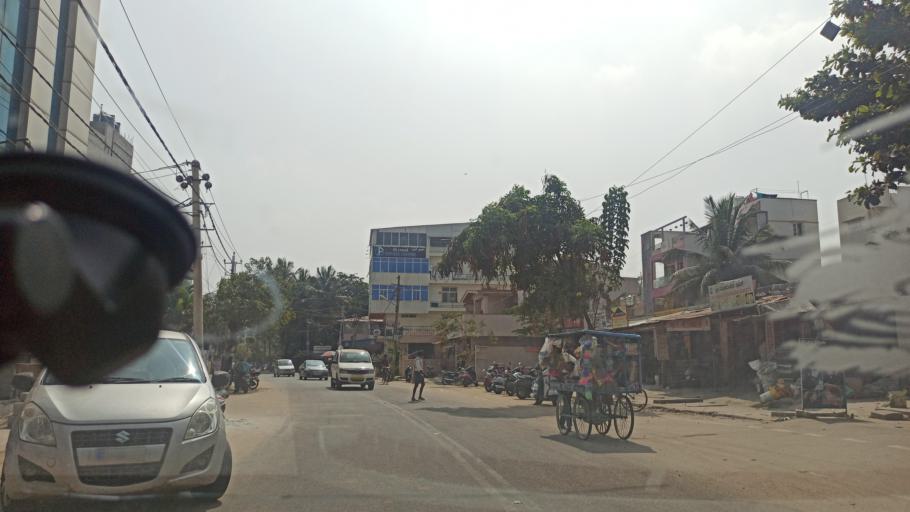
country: IN
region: Karnataka
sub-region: Bangalore Urban
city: Yelahanka
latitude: 13.0934
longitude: 77.6009
